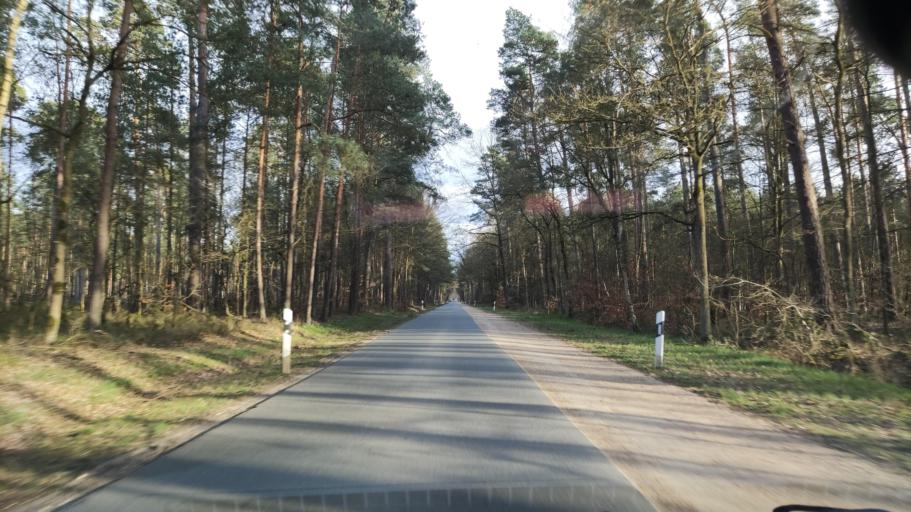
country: DE
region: Lower Saxony
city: Langendorf
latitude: 53.0389
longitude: 11.2518
